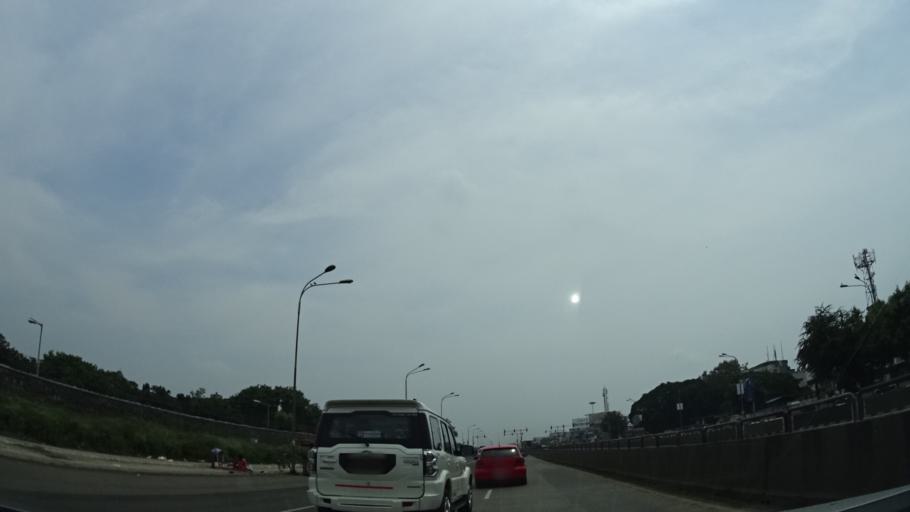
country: IN
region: Maharashtra
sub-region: Pune Division
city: Lohogaon
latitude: 18.5628
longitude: 73.9260
